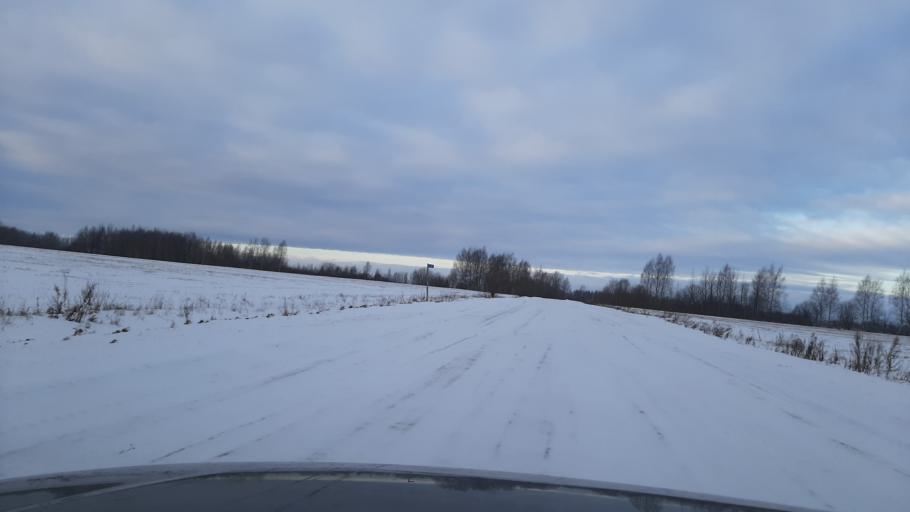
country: RU
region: Kostroma
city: Kosmynino
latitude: 57.4788
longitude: 40.8577
